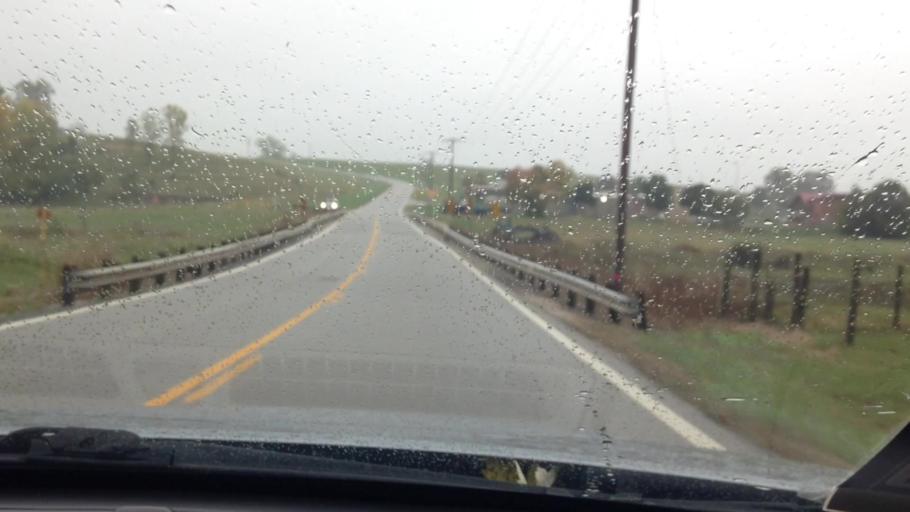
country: US
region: Kansas
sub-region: Leavenworth County
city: Lansing
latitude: 39.2597
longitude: -94.8814
